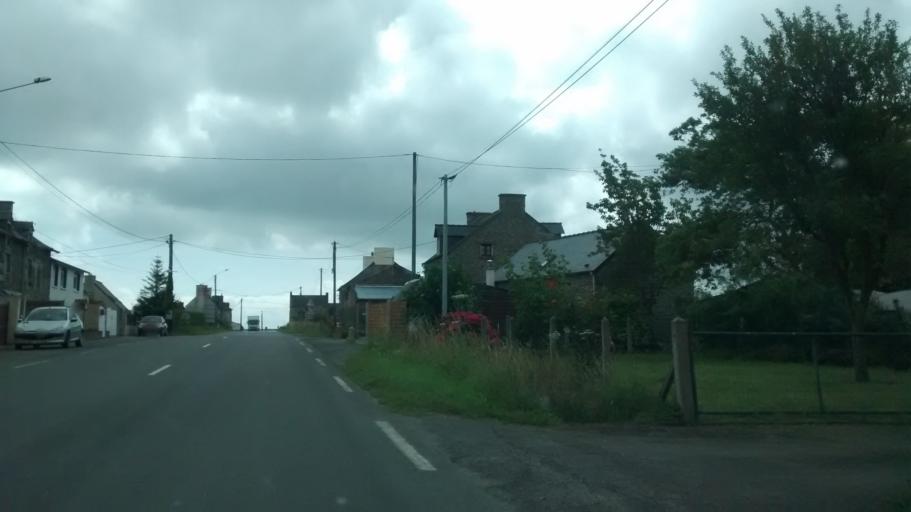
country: FR
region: Brittany
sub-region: Departement d'Ille-et-Vilaine
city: Saint-Meloir-des-Ondes
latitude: 48.6465
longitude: -1.8998
